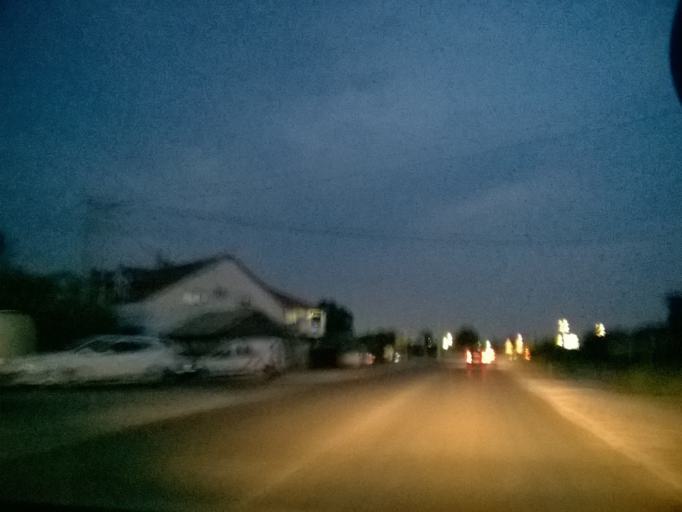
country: ME
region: Podgorica
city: Podgorica
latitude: 42.4382
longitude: 19.2246
